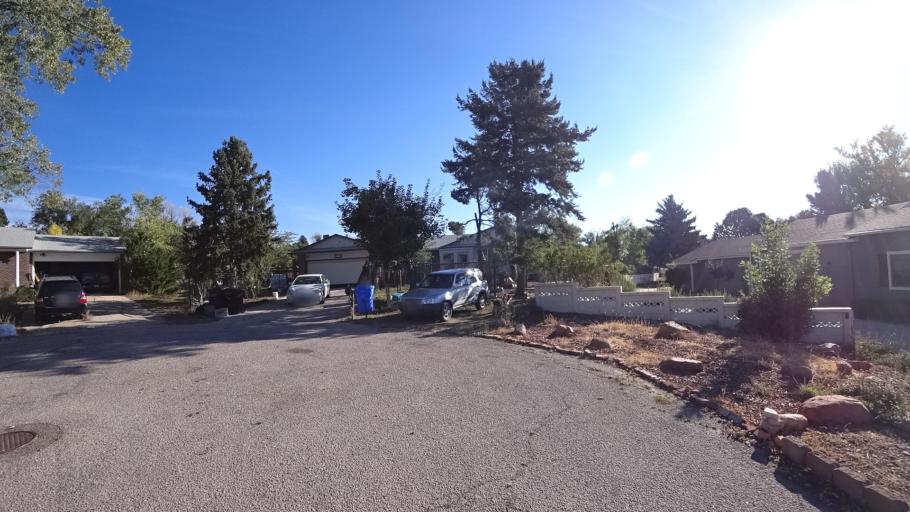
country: US
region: Colorado
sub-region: El Paso County
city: Cimarron Hills
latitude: 38.9071
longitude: -104.7608
